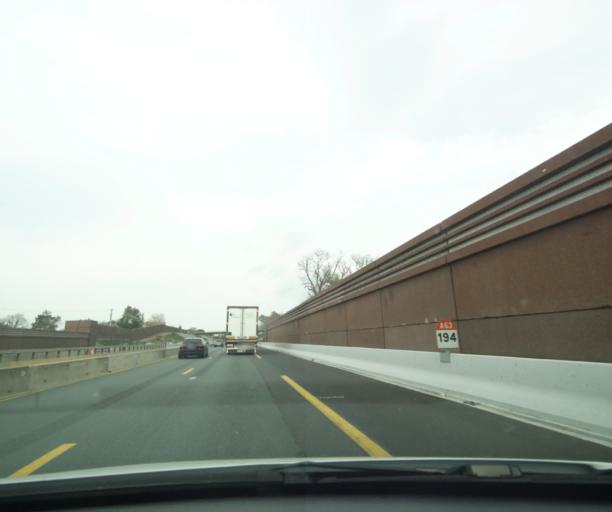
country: FR
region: Aquitaine
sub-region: Departement des Pyrenees-Atlantiques
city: Saint-Jean-de-Luz
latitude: 43.3859
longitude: -1.6424
